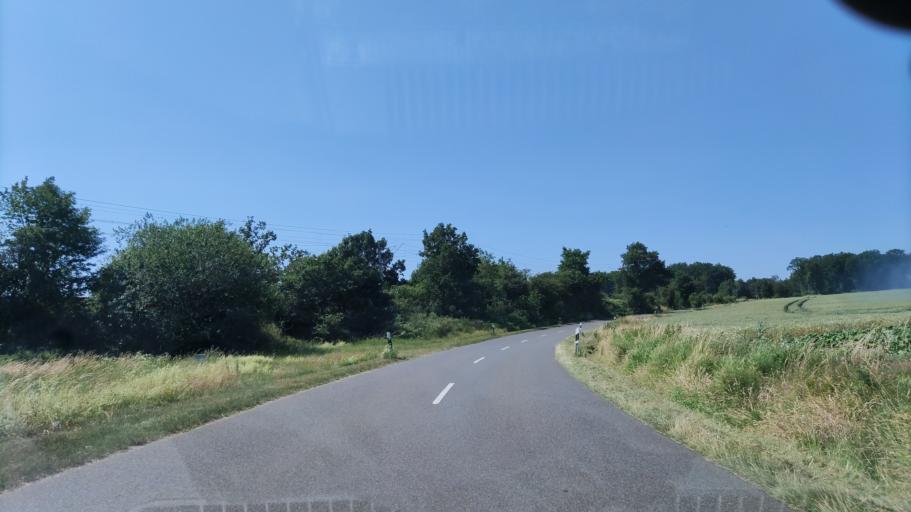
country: DE
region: Lower Saxony
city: Suderburg
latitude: 52.9245
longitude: 10.4698
